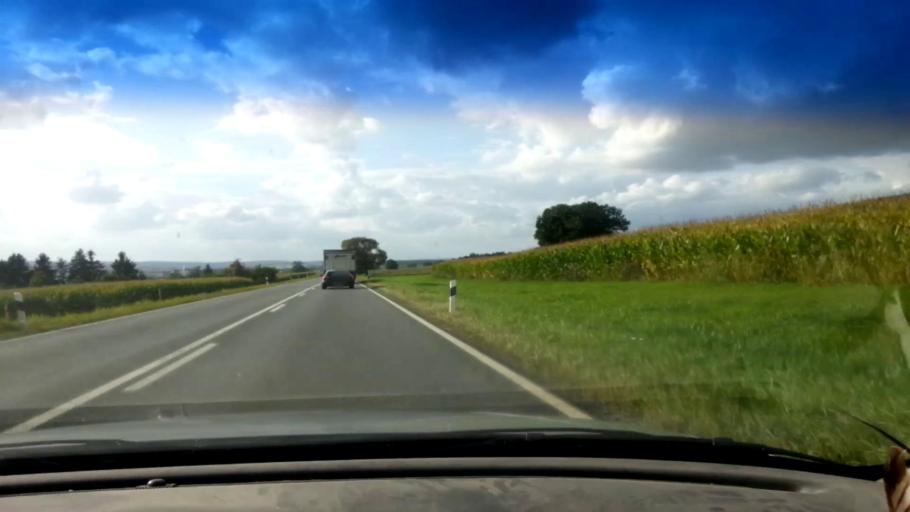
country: DE
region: Bavaria
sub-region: Upper Franconia
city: Gesees
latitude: 50.0495
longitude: 11.6386
